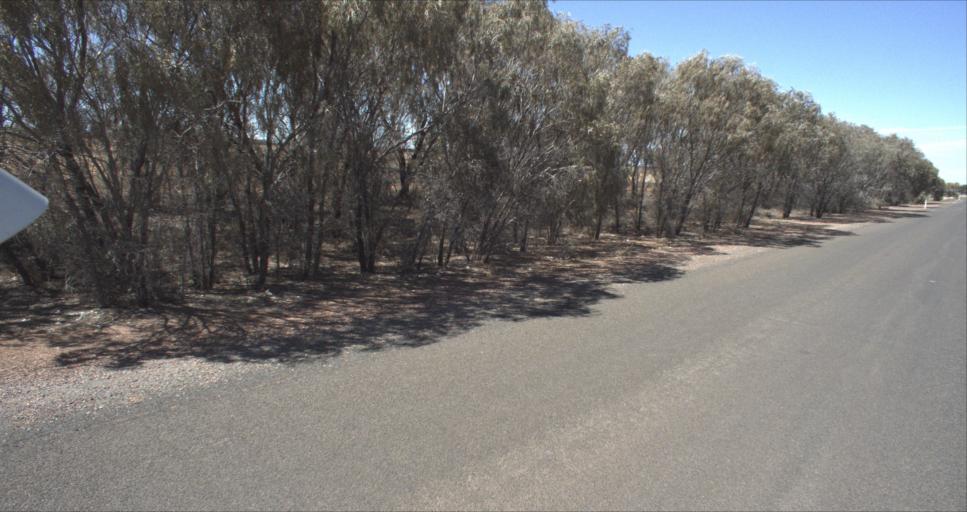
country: AU
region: New South Wales
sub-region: Leeton
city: Leeton
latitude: -34.4859
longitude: 146.2897
